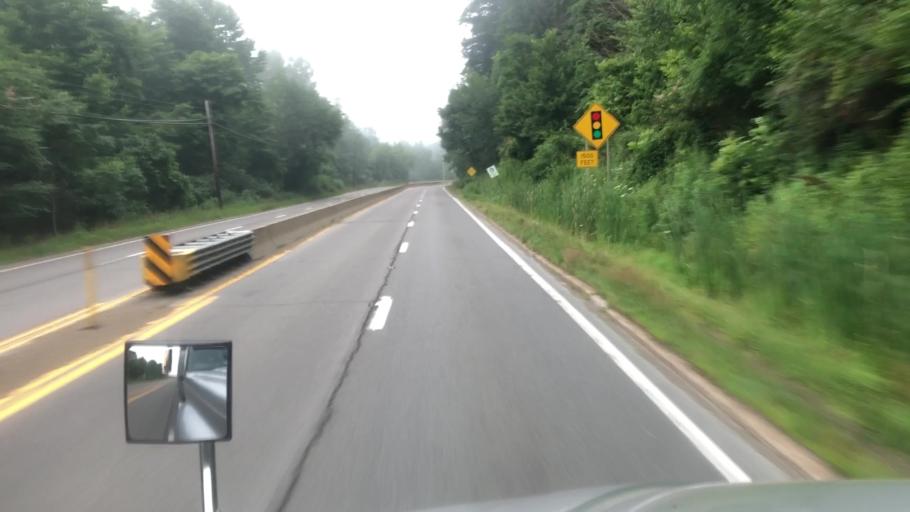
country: US
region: Pennsylvania
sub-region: Venango County
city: Franklin
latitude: 41.3968
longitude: -79.8197
